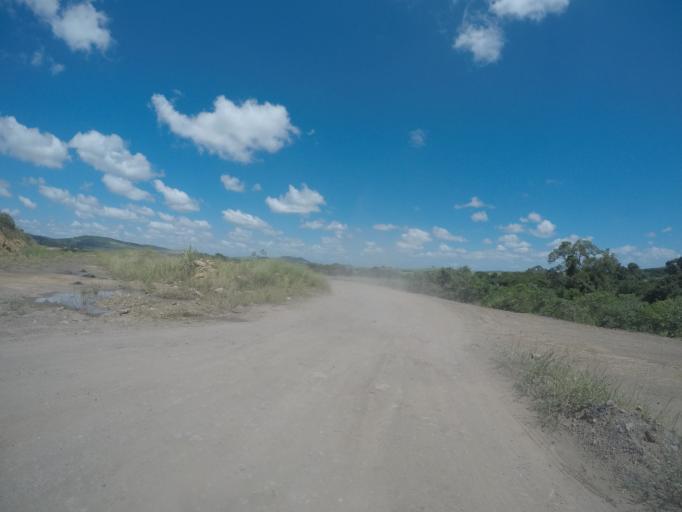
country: ZA
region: KwaZulu-Natal
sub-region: uThungulu District Municipality
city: Empangeni
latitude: -28.6574
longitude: 31.7716
